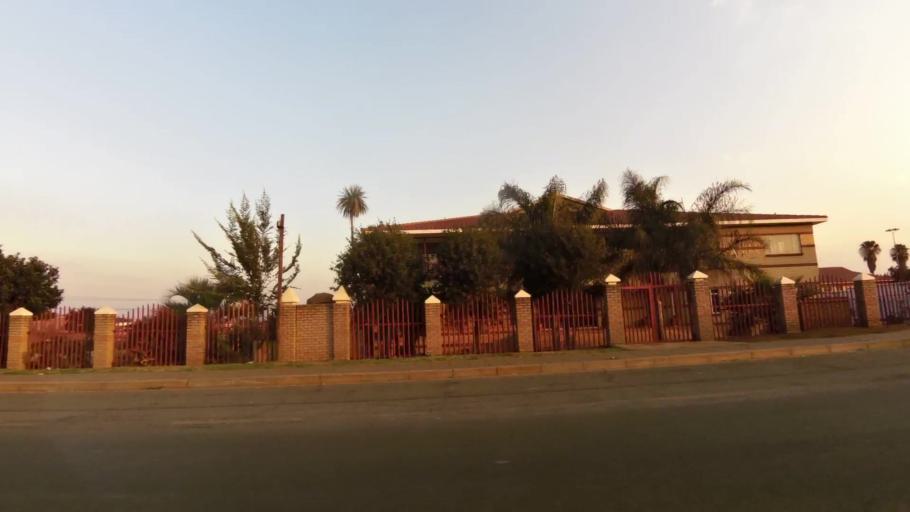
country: ZA
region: Gauteng
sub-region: City of Johannesburg Metropolitan Municipality
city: Soweto
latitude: -26.2894
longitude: 27.9036
